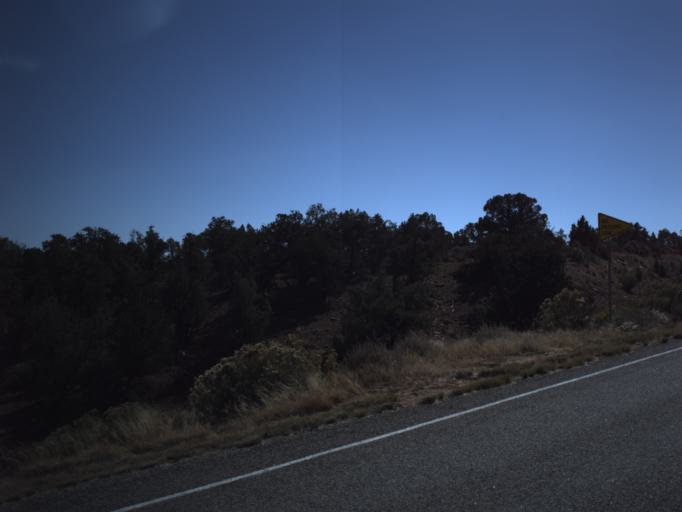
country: US
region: Utah
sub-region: San Juan County
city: Blanding
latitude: 37.5769
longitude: -110.0384
